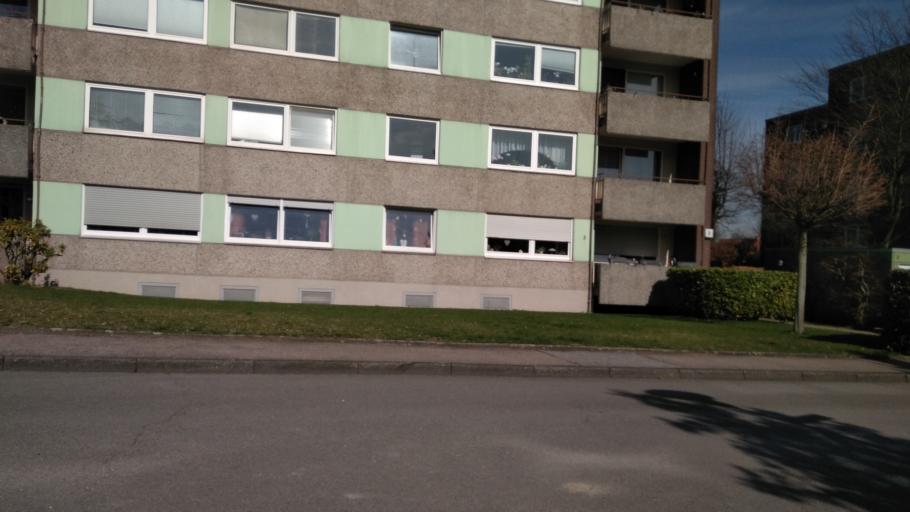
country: DE
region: North Rhine-Westphalia
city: Dorsten
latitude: 51.6088
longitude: 6.9234
